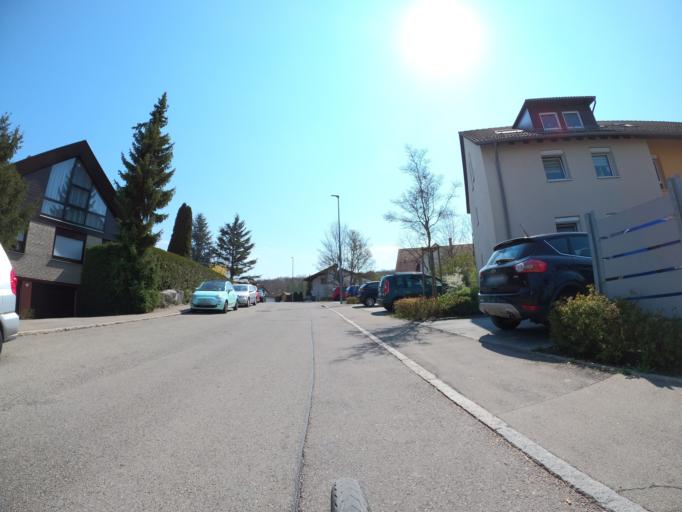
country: DE
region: Baden-Wuerttemberg
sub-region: Tuebingen Region
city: Wannweil
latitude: 48.4736
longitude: 9.1440
